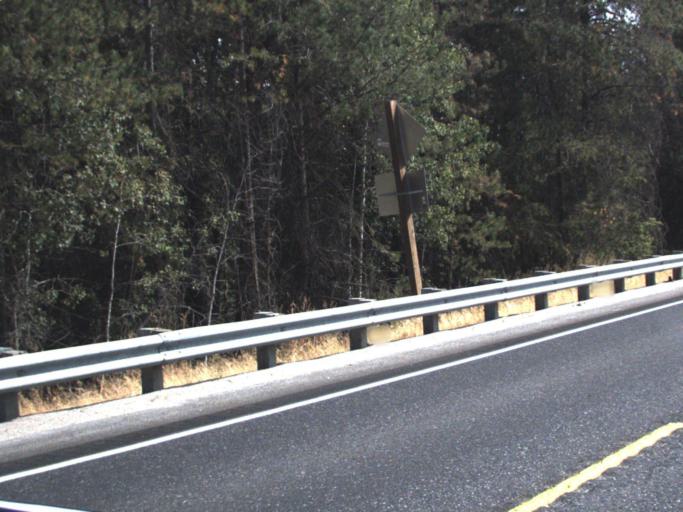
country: US
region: Washington
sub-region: Spokane County
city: Deer Park
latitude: 48.0130
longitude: -117.5845
